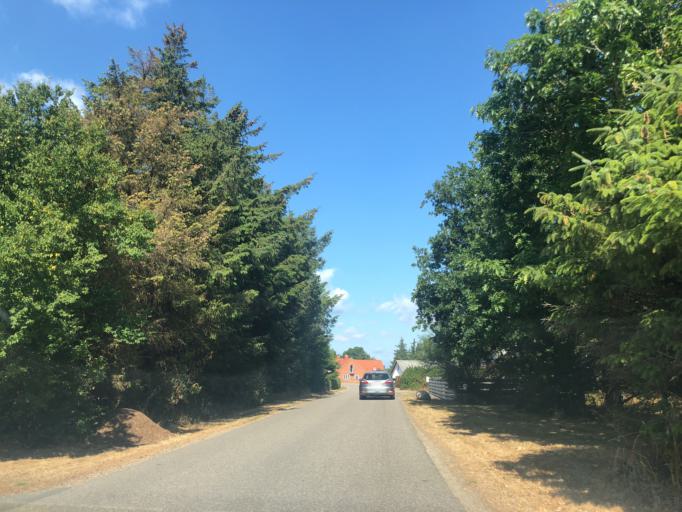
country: DK
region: North Denmark
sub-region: Morso Kommune
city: Nykobing Mors
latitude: 56.8024
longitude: 9.0012
